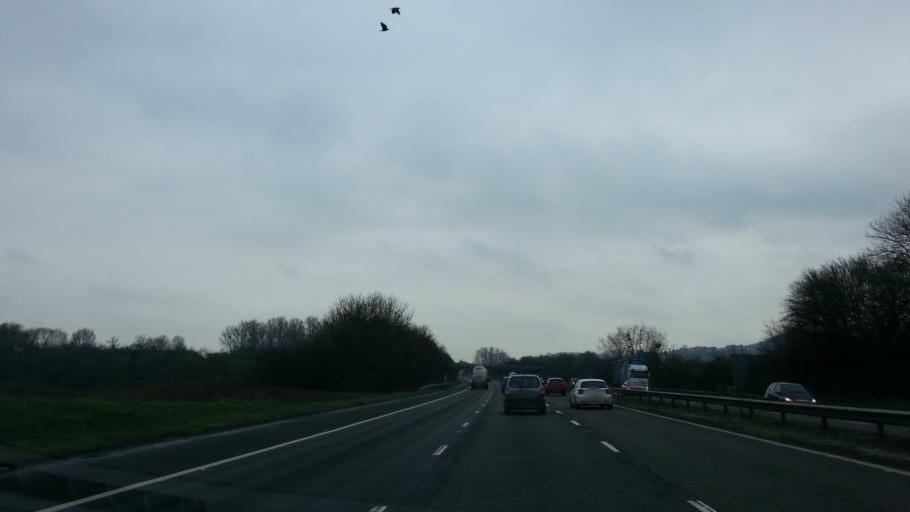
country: GB
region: England
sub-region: South Gloucestershire
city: Charfield
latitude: 51.6716
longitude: -2.4069
